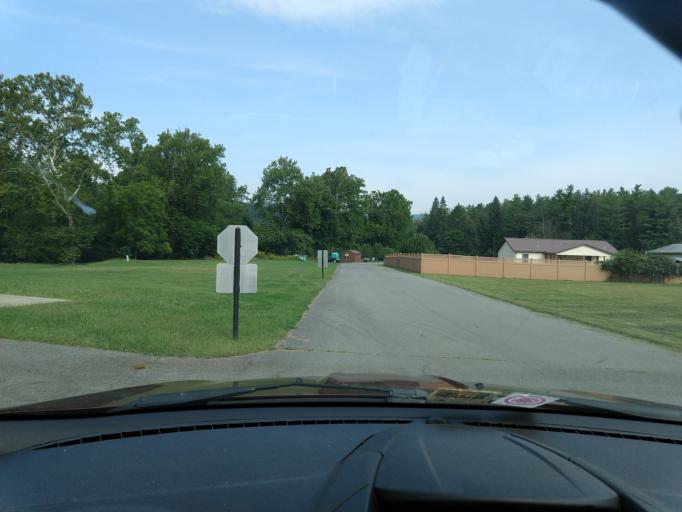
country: US
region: Virginia
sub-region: City of Covington
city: Covington
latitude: 37.9642
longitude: -80.1284
